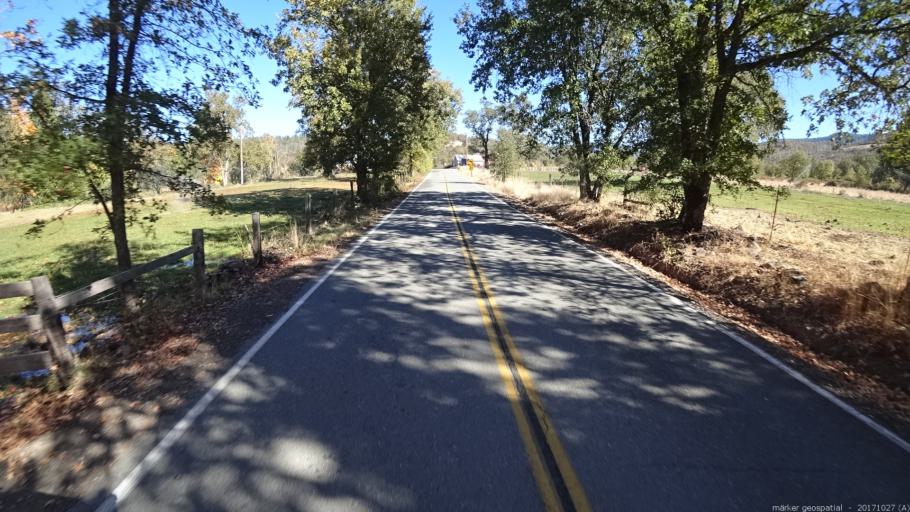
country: US
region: California
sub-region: Shasta County
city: Bella Vista
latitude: 40.7409
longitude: -121.9946
